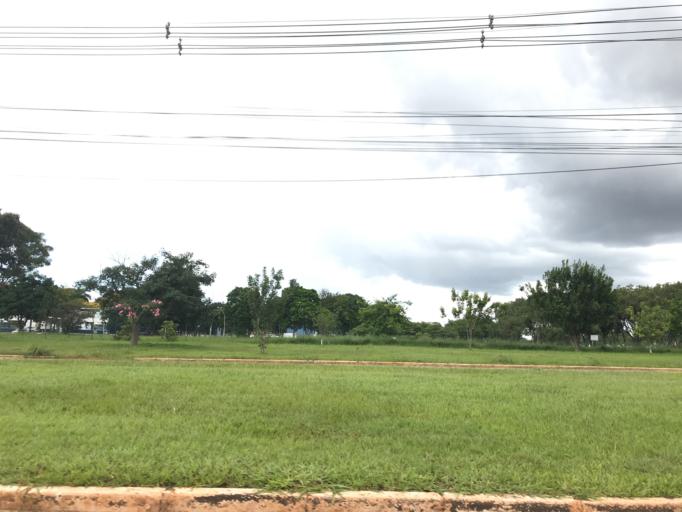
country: BR
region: Federal District
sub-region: Brasilia
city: Brasilia
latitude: -15.8271
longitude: -47.9338
